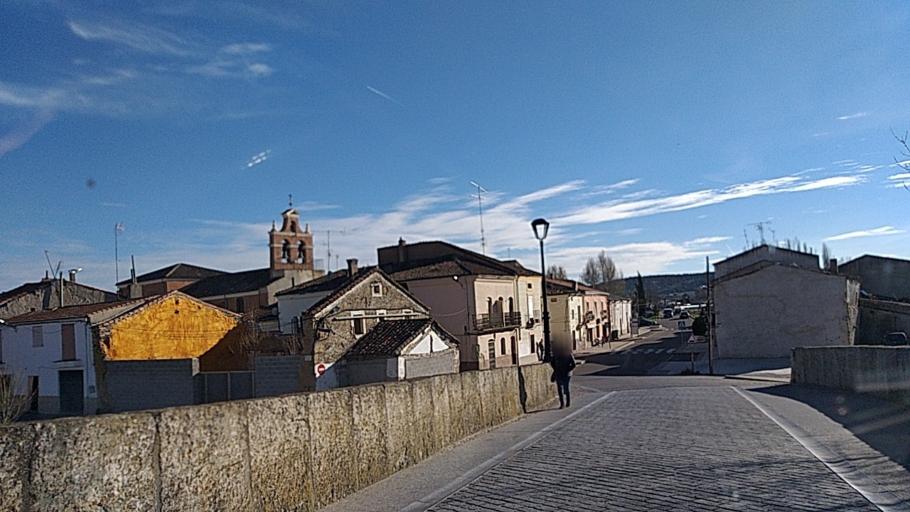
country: ES
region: Castille and Leon
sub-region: Provincia de Salamanca
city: Ciudad Rodrigo
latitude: 40.5944
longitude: -6.5378
